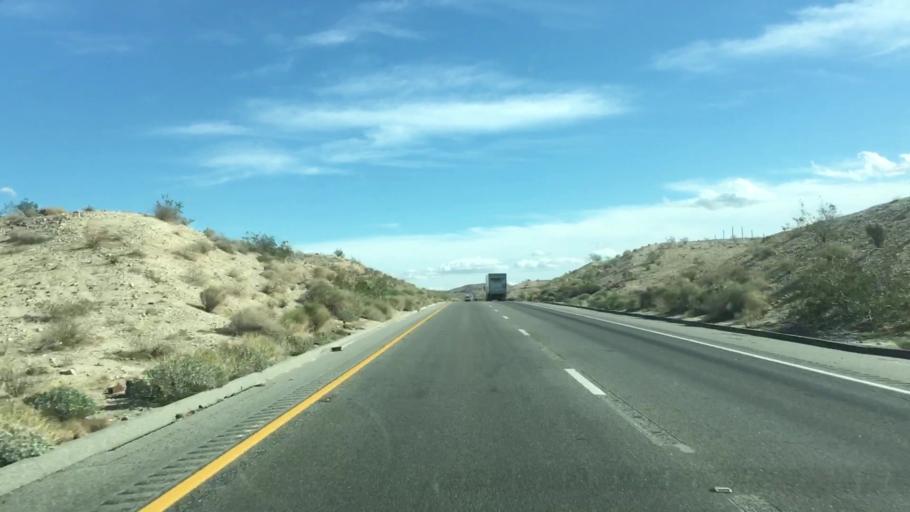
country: US
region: California
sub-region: Riverside County
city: Mecca
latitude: 33.6836
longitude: -116.0164
